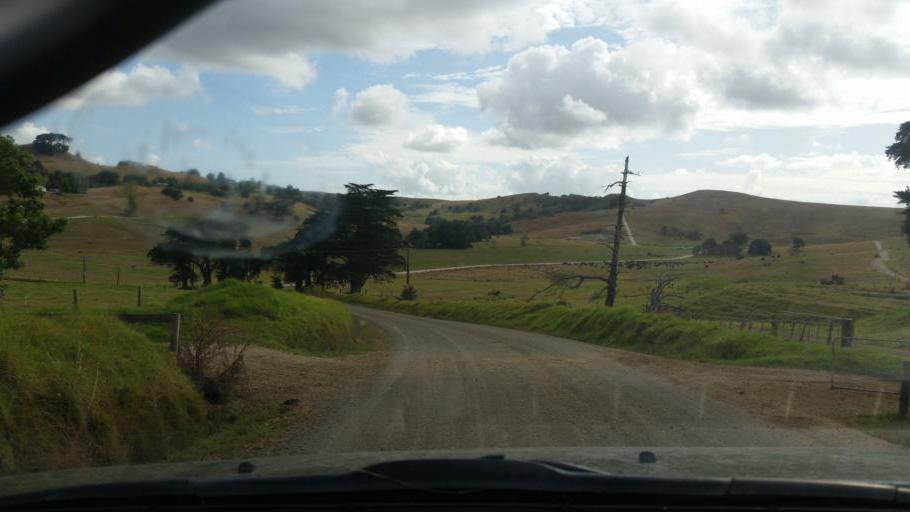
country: NZ
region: Northland
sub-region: Kaipara District
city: Dargaville
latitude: -36.0053
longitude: 173.9480
